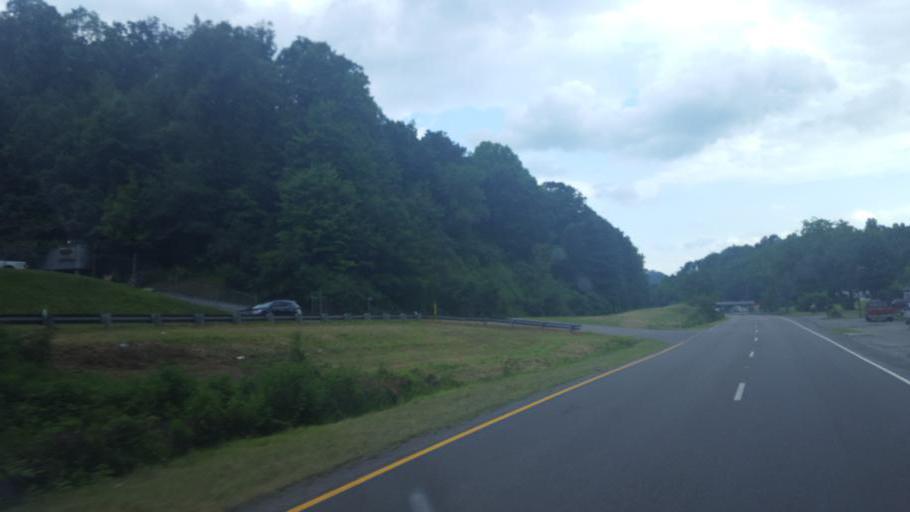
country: US
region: Virginia
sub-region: Wise County
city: Pound
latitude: 37.0933
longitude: -82.6002
